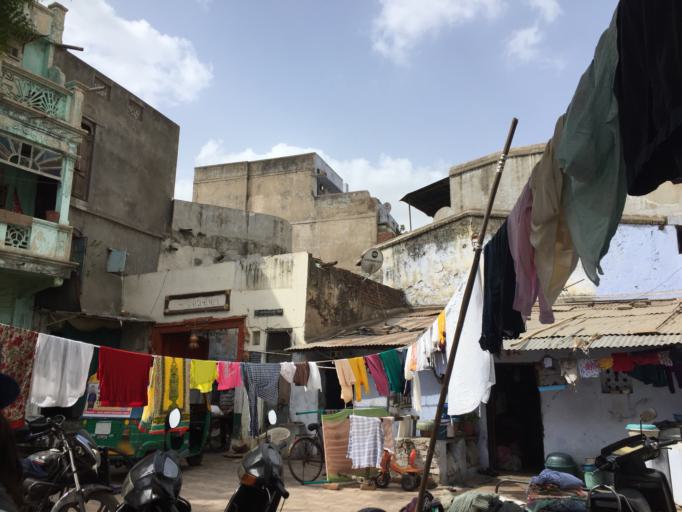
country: IN
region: Gujarat
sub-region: Ahmadabad
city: Ahmedabad
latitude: 23.0376
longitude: 72.5852
